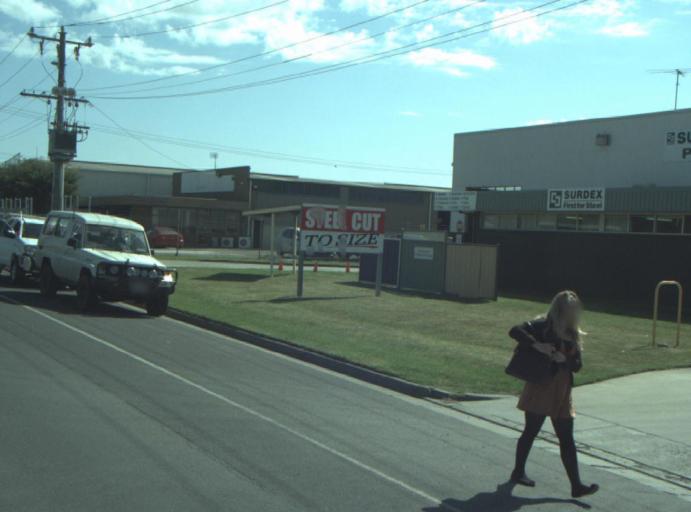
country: AU
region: Victoria
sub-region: Greater Geelong
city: Geelong West
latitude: -38.1236
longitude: 144.3468
